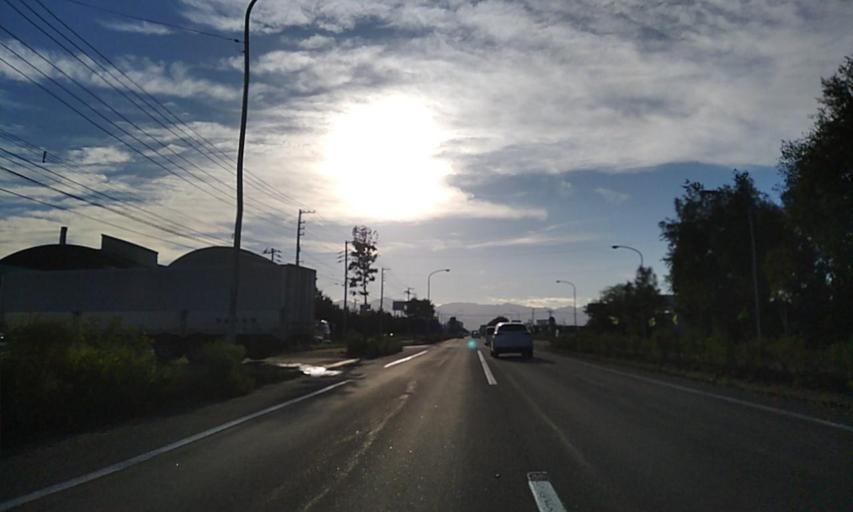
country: JP
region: Hokkaido
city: Obihiro
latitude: 42.9241
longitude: 143.0995
